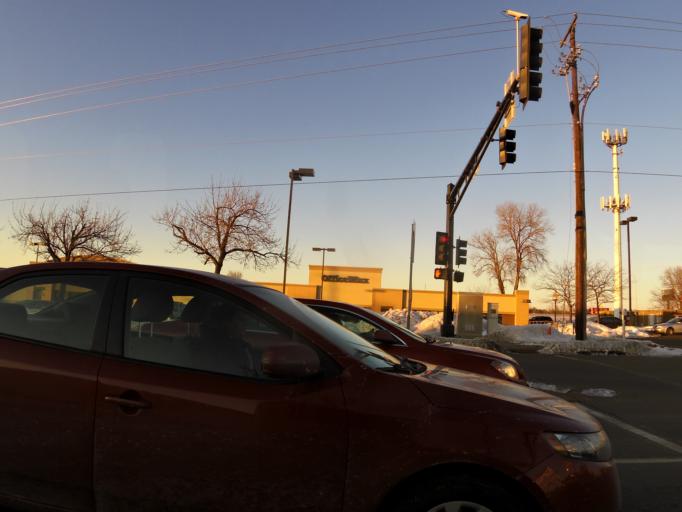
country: US
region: Minnesota
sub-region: Ramsey County
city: North Saint Paul
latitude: 45.0357
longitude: -93.0223
